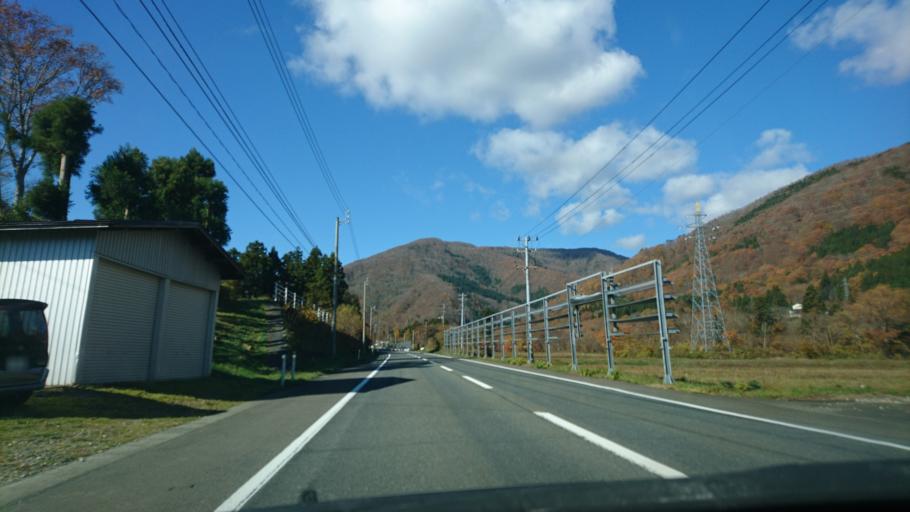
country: JP
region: Iwate
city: Kitakami
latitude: 39.3078
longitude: 140.9162
